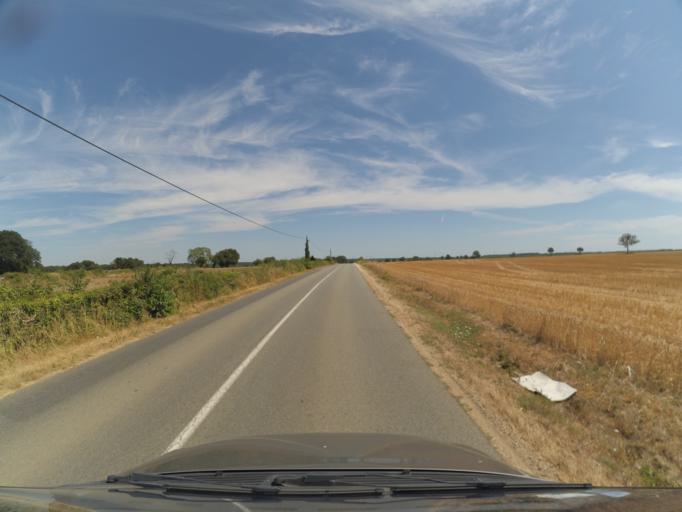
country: FR
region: Poitou-Charentes
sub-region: Departement de la Vienne
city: Vivonne
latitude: 46.4225
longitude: 0.2898
